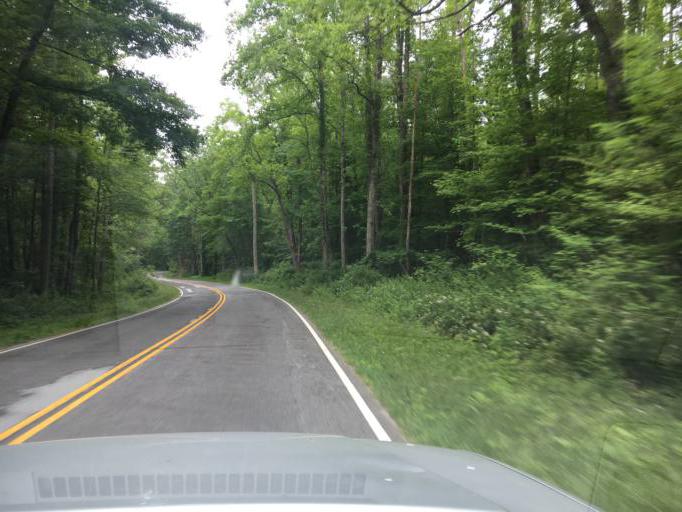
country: US
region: North Carolina
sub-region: Henderson County
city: Flat Rock
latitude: 35.1808
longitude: -82.4097
